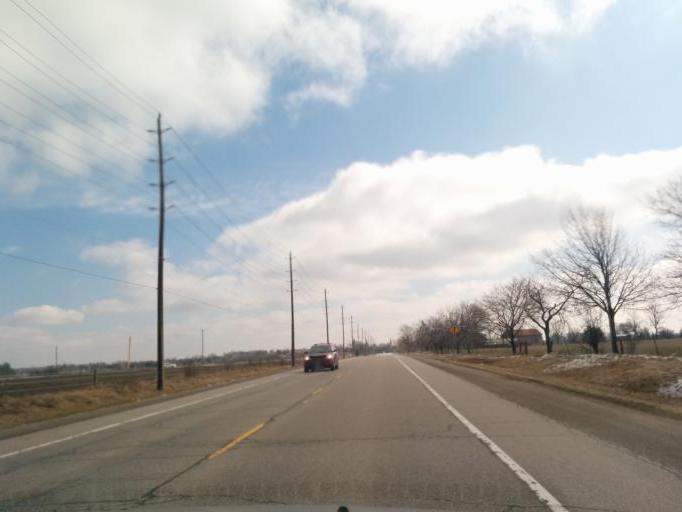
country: CA
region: Ontario
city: Waterloo
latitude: 43.5181
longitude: -80.4641
